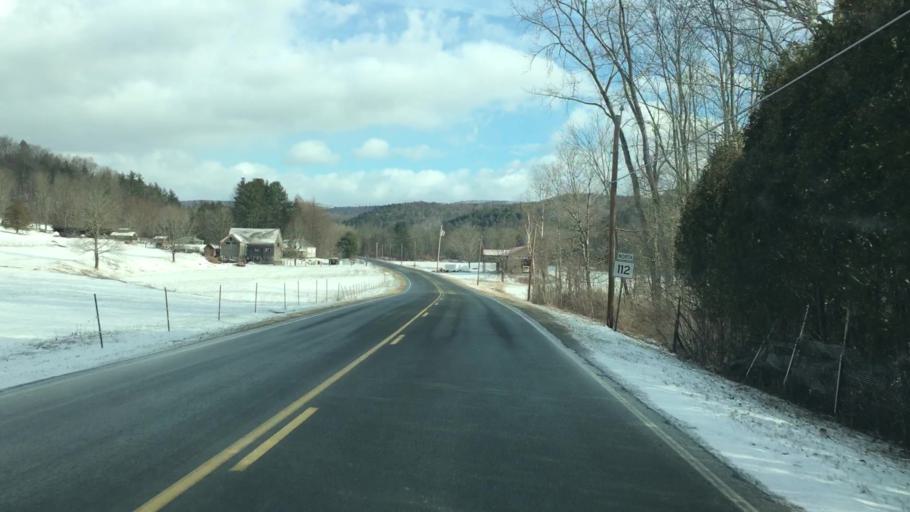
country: US
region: Massachusetts
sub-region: Franklin County
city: Colrain
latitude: 42.7120
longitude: -72.7039
